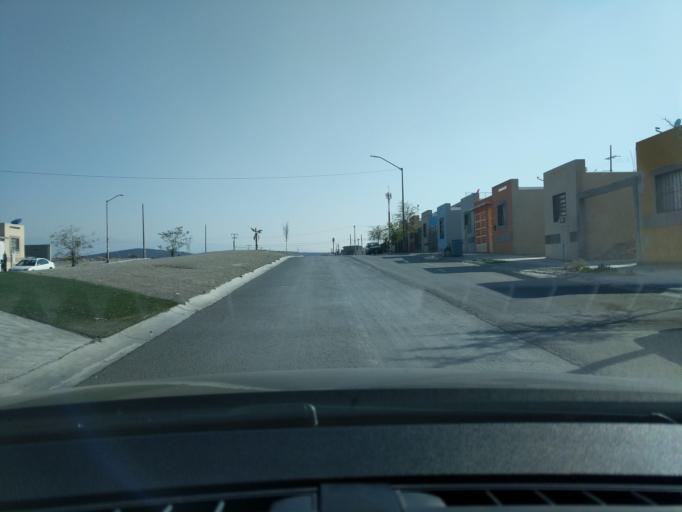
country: MX
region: Coahuila
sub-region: Ramos Arizpe
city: Ramos Arizpe
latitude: 25.5491
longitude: -100.9670
